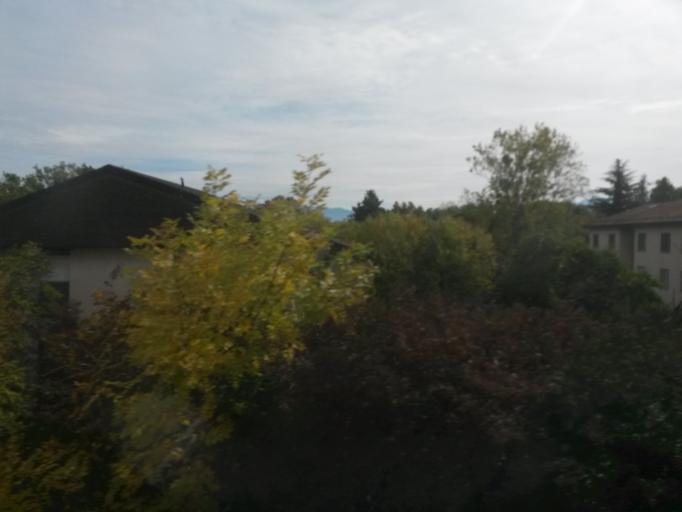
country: CH
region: Vaud
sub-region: Morges District
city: Saint-Prex
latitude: 46.4871
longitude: 6.4608
